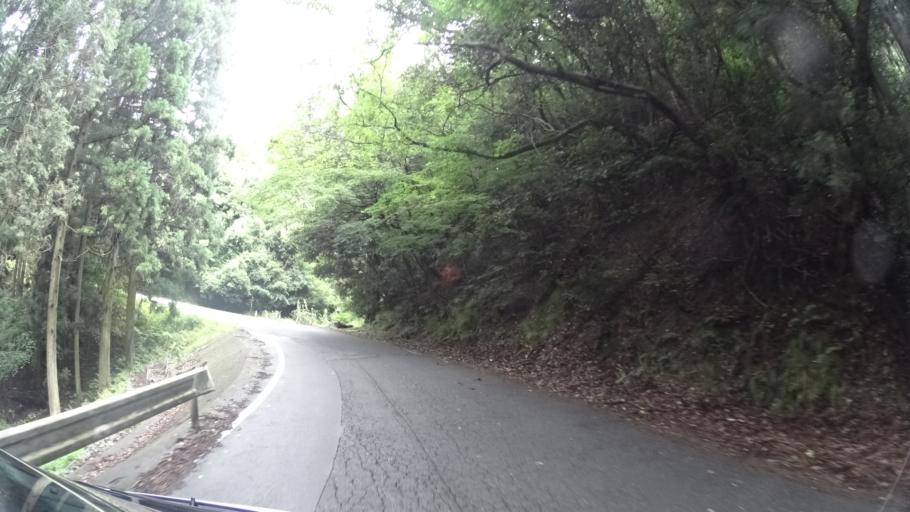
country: JP
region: Kyoto
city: Kameoka
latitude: 35.0520
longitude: 135.4220
